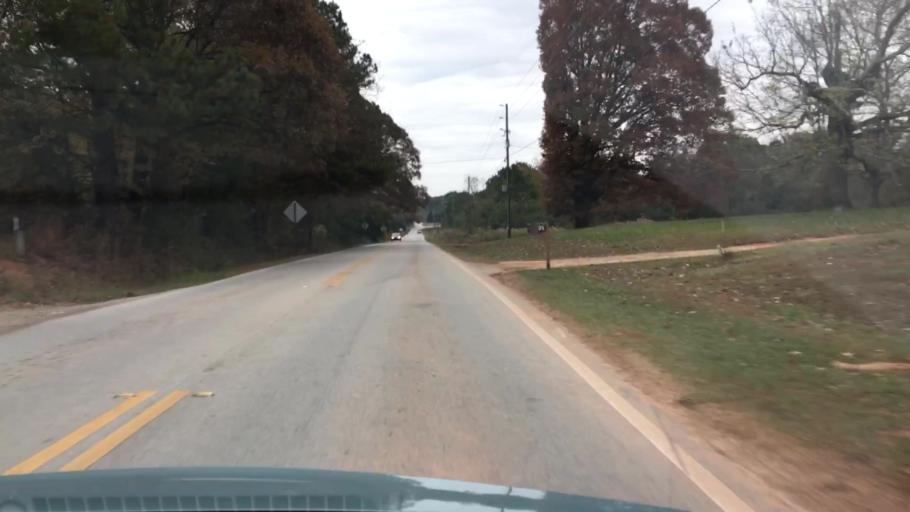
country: US
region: Georgia
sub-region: Henry County
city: McDonough
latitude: 33.5074
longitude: -84.1153
